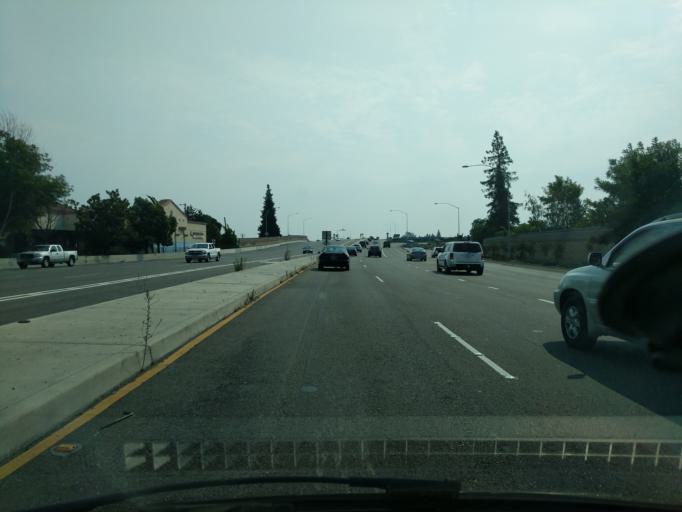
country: US
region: California
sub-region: Alameda County
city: Hayward
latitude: 37.6486
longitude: -122.0918
